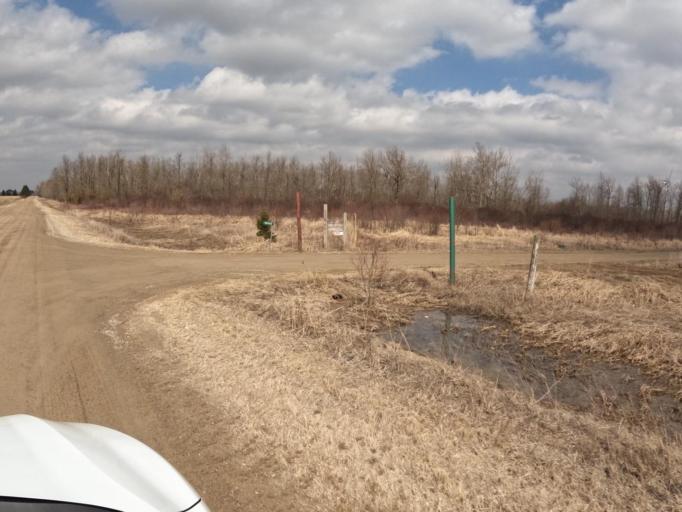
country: CA
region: Ontario
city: Shelburne
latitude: 44.0230
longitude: -80.3302
